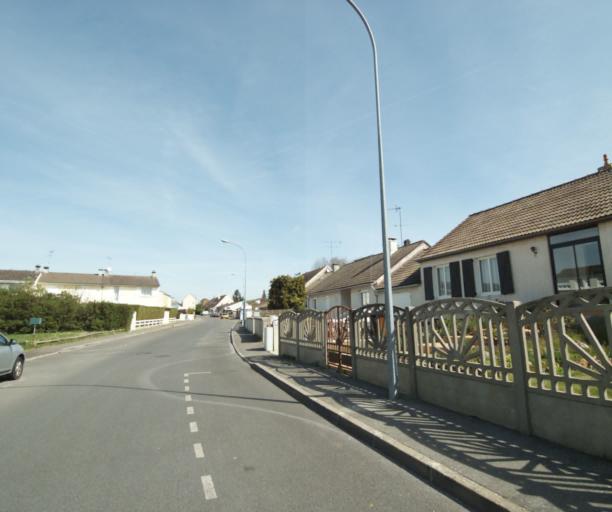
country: FR
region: Ile-de-France
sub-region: Departement de Seine-et-Marne
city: Nangis
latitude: 48.5527
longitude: 3.0228
